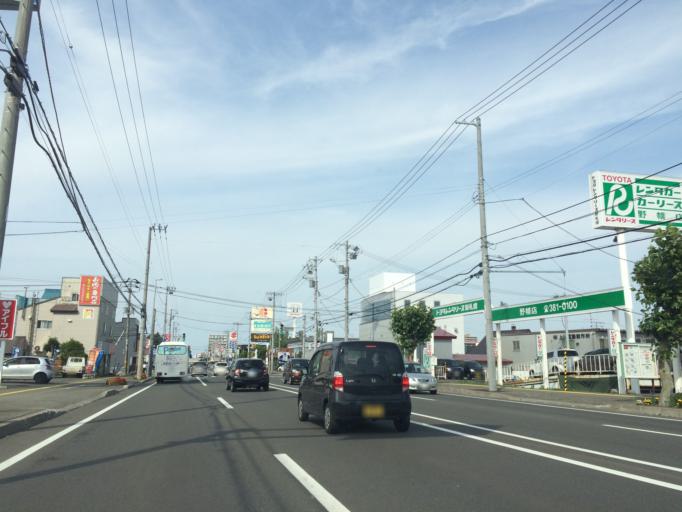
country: JP
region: Hokkaido
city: Ebetsu
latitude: 43.0893
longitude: 141.5181
